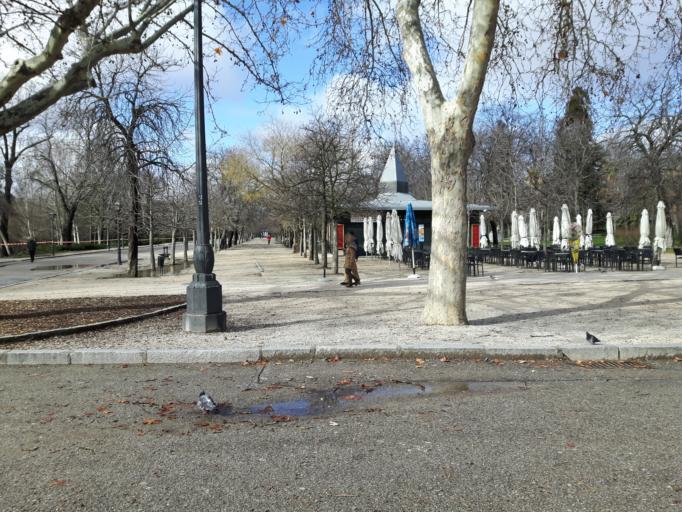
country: ES
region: Madrid
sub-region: Provincia de Madrid
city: Retiro
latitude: 40.4164
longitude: -3.6802
